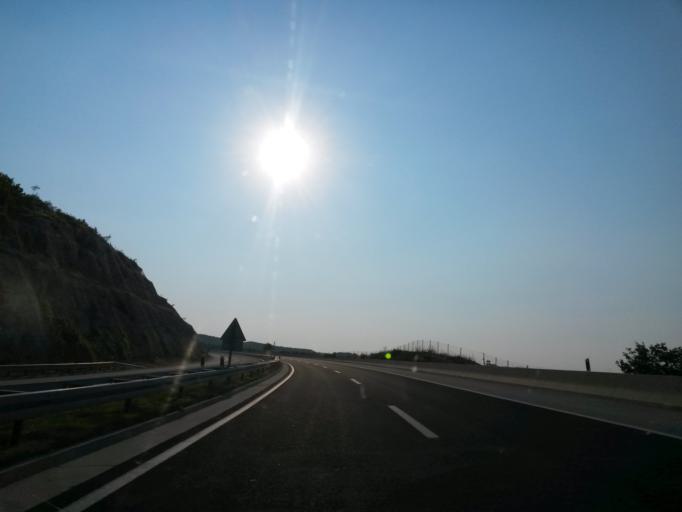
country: HR
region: Splitsko-Dalmatinska
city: Greda
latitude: 43.5819
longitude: 16.6595
